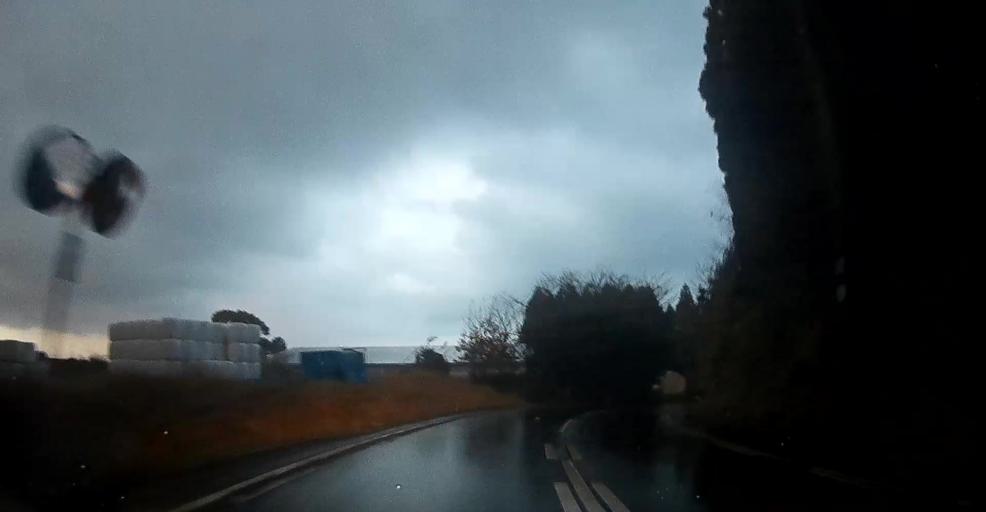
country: JP
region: Kumamoto
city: Ozu
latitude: 32.8187
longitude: 130.9151
